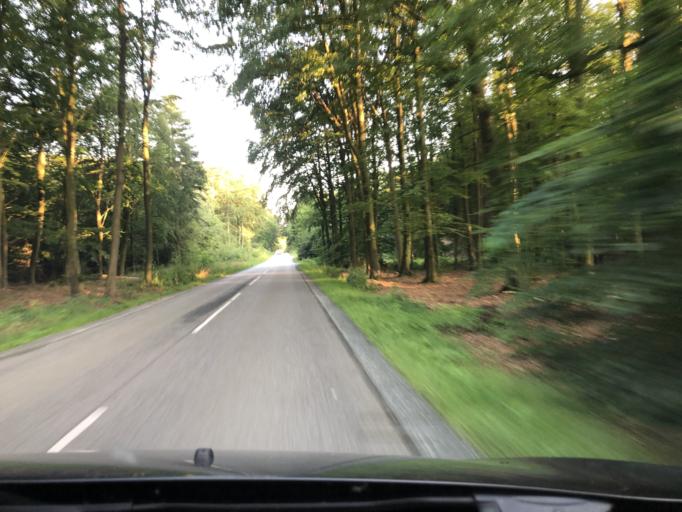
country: DK
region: South Denmark
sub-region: Vejle Kommune
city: Borkop
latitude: 55.6816
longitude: 9.6153
